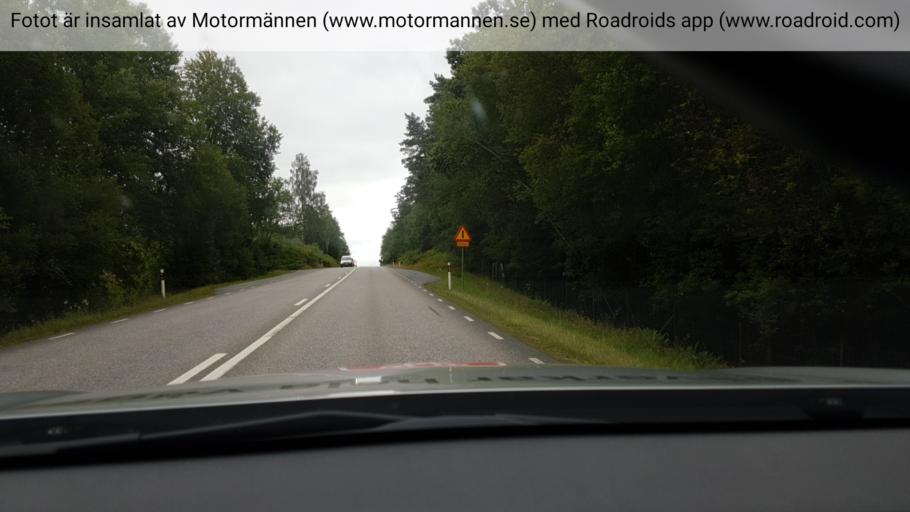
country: SE
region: Vaestra Goetaland
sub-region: Harryda Kommun
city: Ravlanda
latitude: 57.5658
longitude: 12.5120
